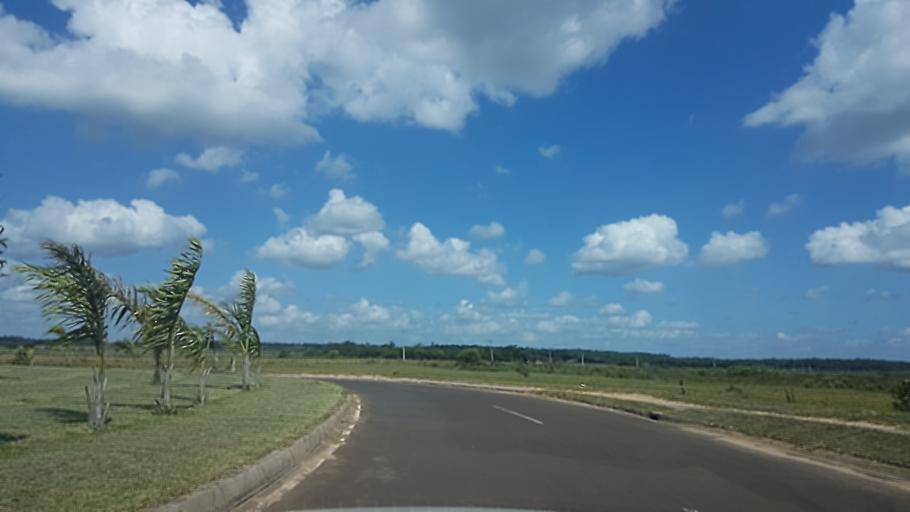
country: PY
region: Itapua
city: Carmen del Parana
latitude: -27.2281
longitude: -56.1375
